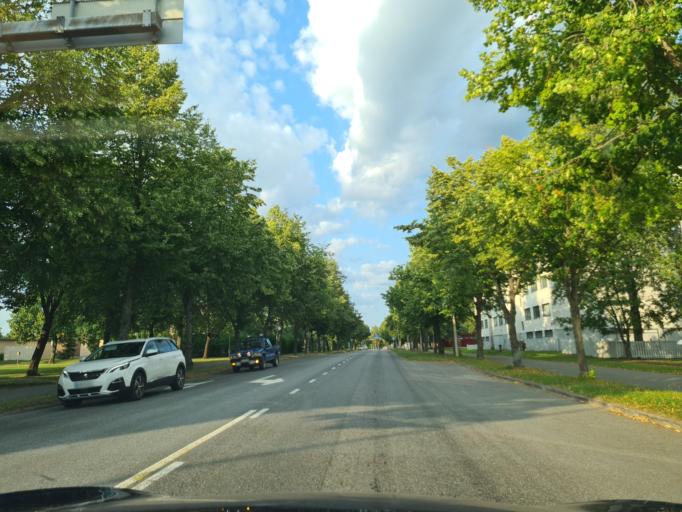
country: FI
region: Southern Ostrobothnia
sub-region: Seinaejoki
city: Lapua
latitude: 62.9721
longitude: 23.0028
